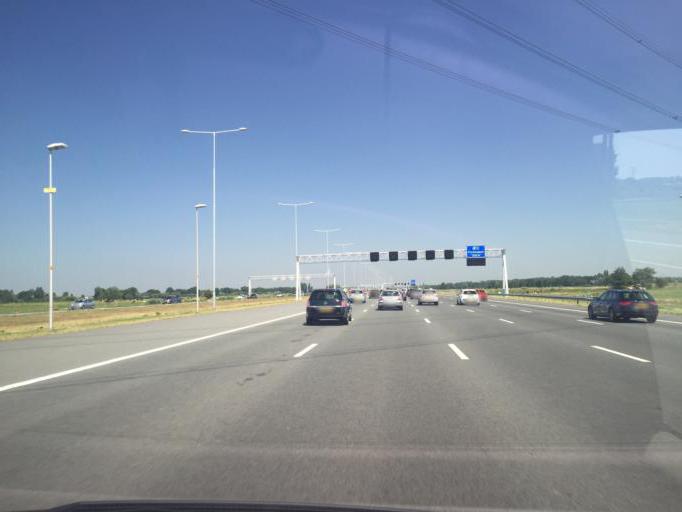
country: NL
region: Utrecht
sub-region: Stichtse Vecht
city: Breukelen
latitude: 52.2099
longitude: 4.9870
